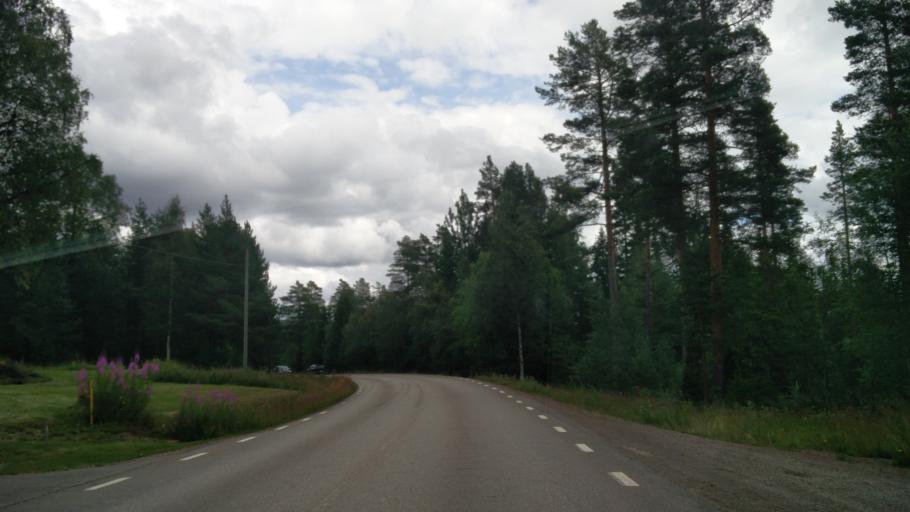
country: NO
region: Hedmark
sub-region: Trysil
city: Innbygda
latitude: 61.1757
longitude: 12.8665
